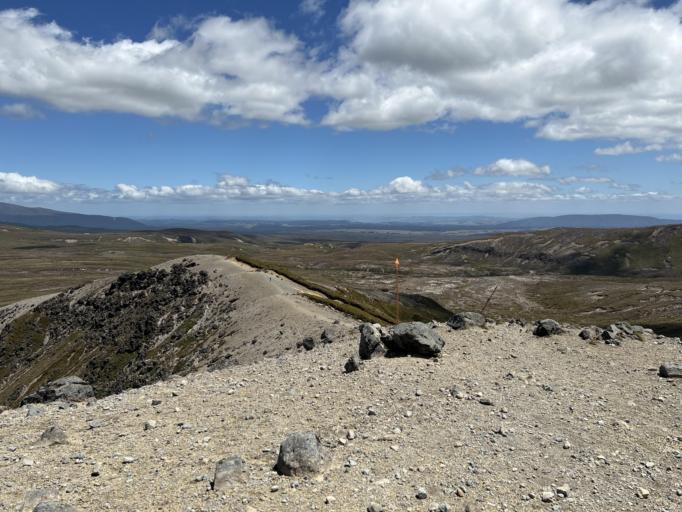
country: NZ
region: Waikato
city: Turangi
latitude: -39.1898
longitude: 175.6121
